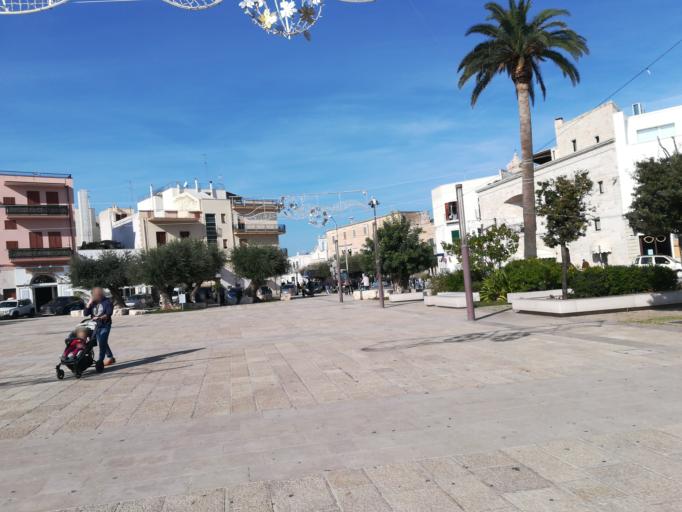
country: IT
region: Apulia
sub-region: Provincia di Bari
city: Polignano a Mare
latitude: 40.9946
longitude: 17.2201
